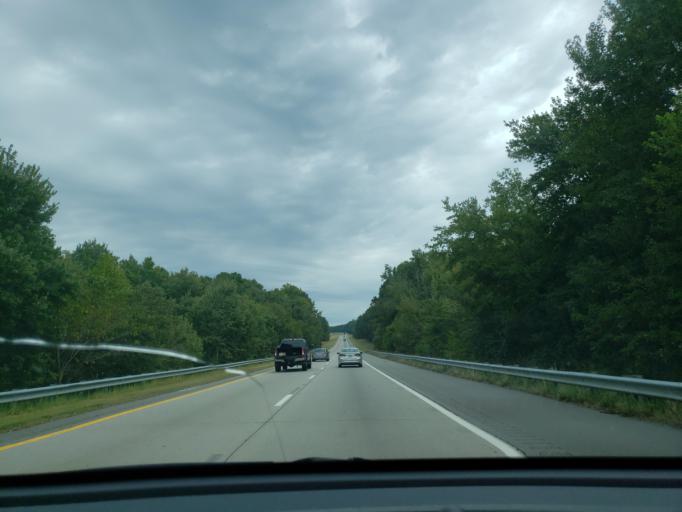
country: US
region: North Carolina
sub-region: Granville County
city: Creedmoor
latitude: 36.1815
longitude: -78.6957
